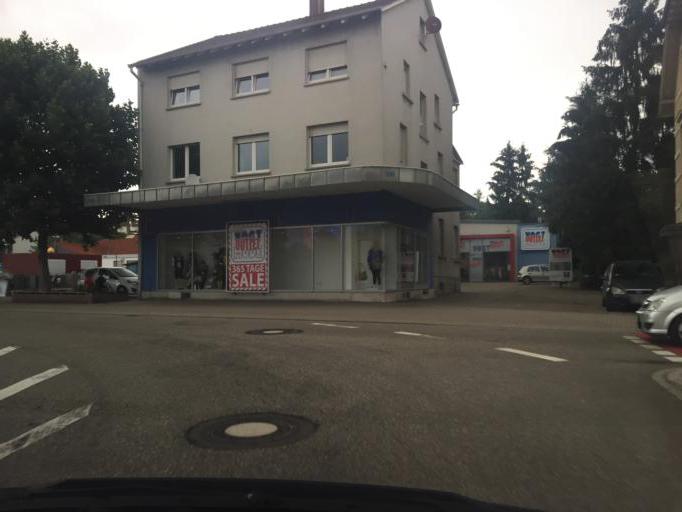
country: DE
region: Baden-Wuerttemberg
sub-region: Karlsruhe Region
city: Bretten
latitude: 49.0383
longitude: 8.6983
